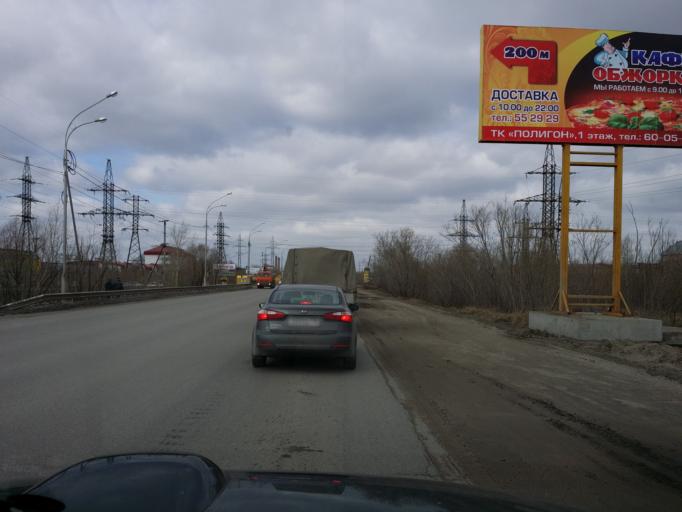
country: RU
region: Khanty-Mansiyskiy Avtonomnyy Okrug
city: Nizhnevartovsk
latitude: 60.9318
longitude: 76.5313
